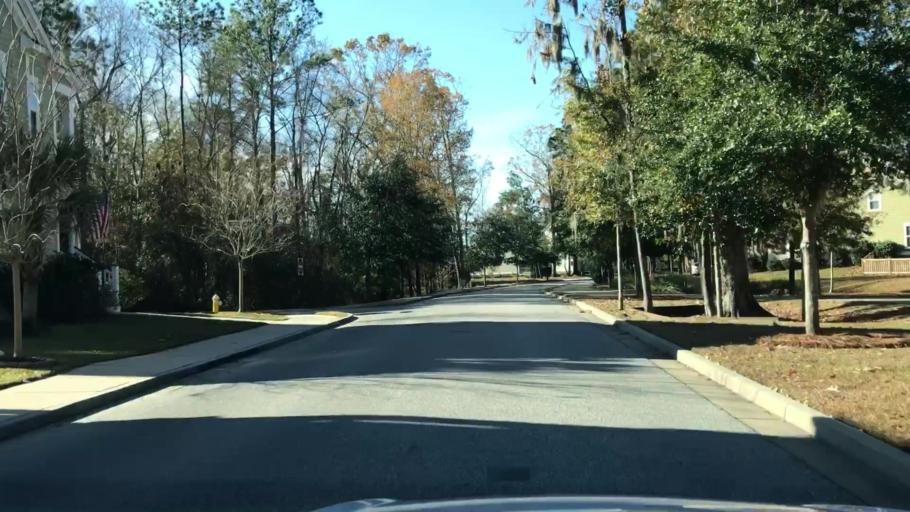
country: US
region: South Carolina
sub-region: Charleston County
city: Shell Point
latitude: 32.8080
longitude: -80.0546
